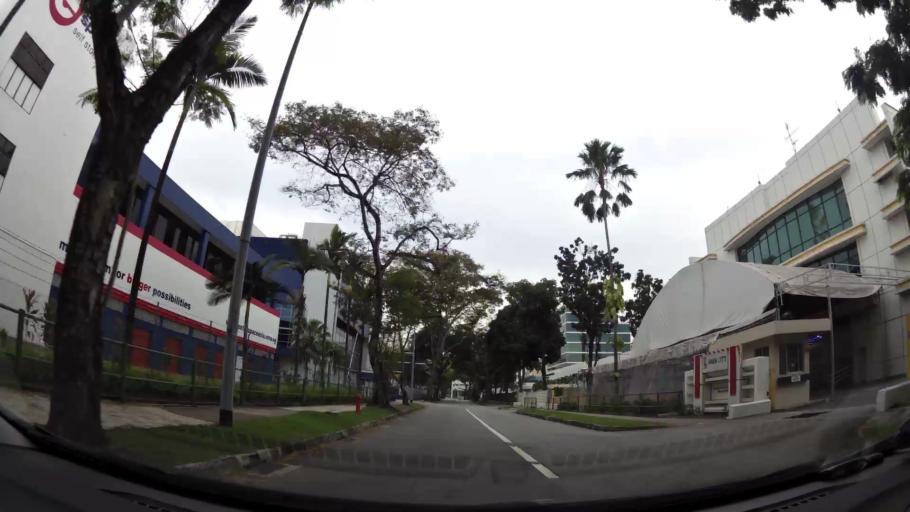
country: SG
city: Singapore
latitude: 1.3721
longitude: 103.8644
